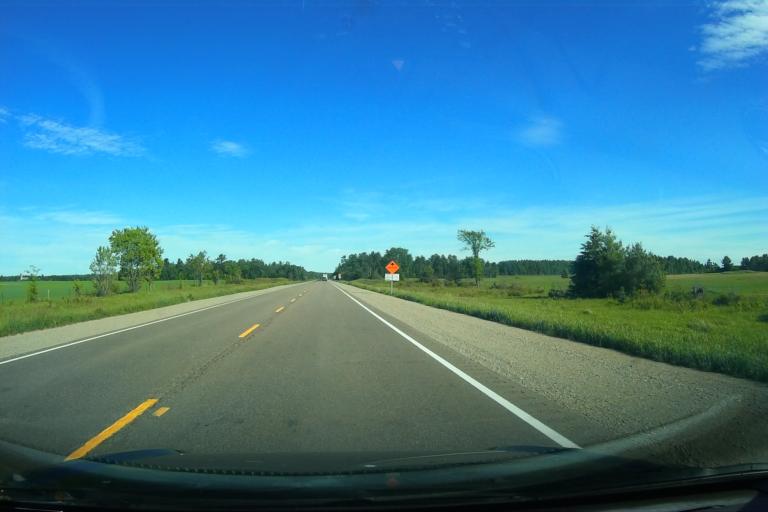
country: CA
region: Ontario
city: Pembroke
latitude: 45.7802
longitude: -77.0968
